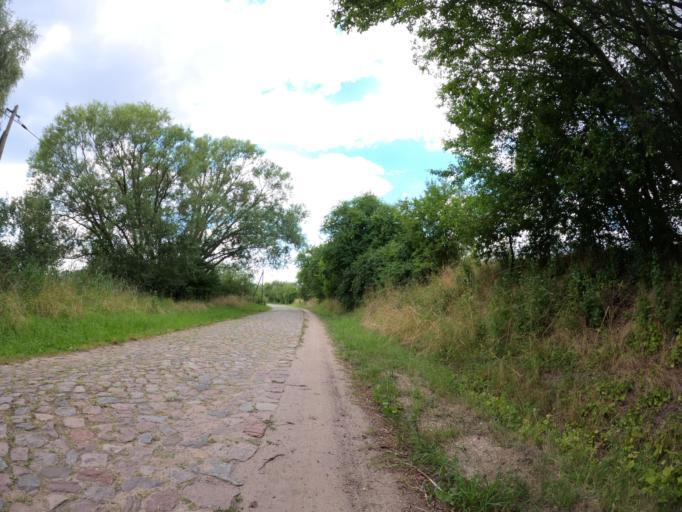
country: DE
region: Mecklenburg-Vorpommern
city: Woldegk
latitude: 53.4129
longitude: 13.6196
